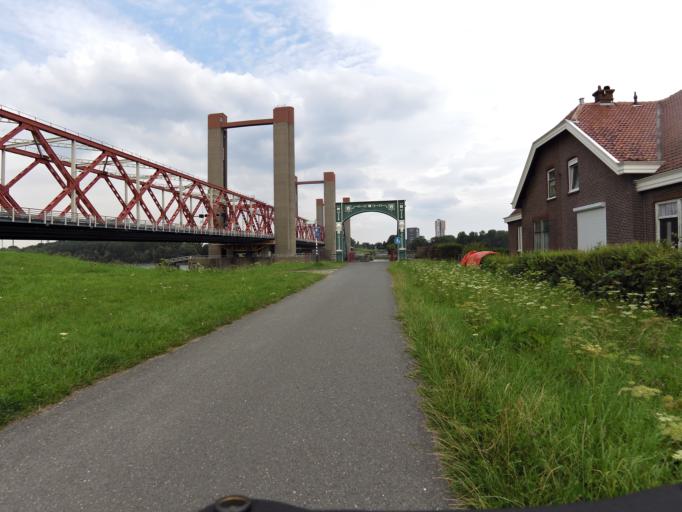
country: NL
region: South Holland
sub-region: Gemeente Spijkenisse
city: Spijkenisse
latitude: 51.8581
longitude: 4.3378
